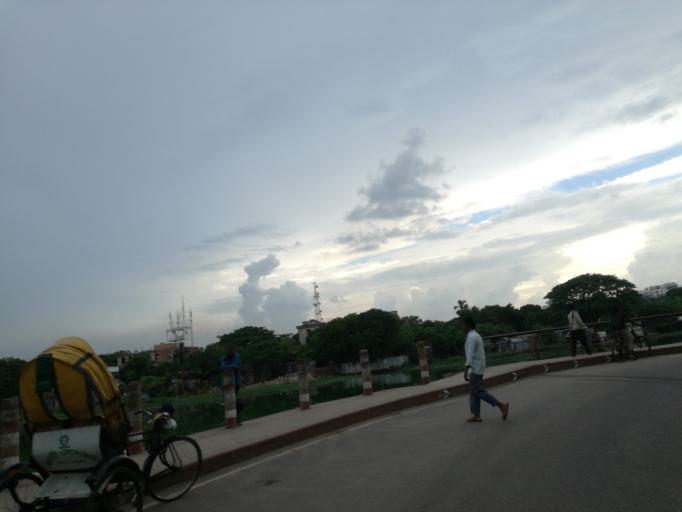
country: BD
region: Dhaka
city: Paltan
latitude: 23.7874
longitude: 90.4144
